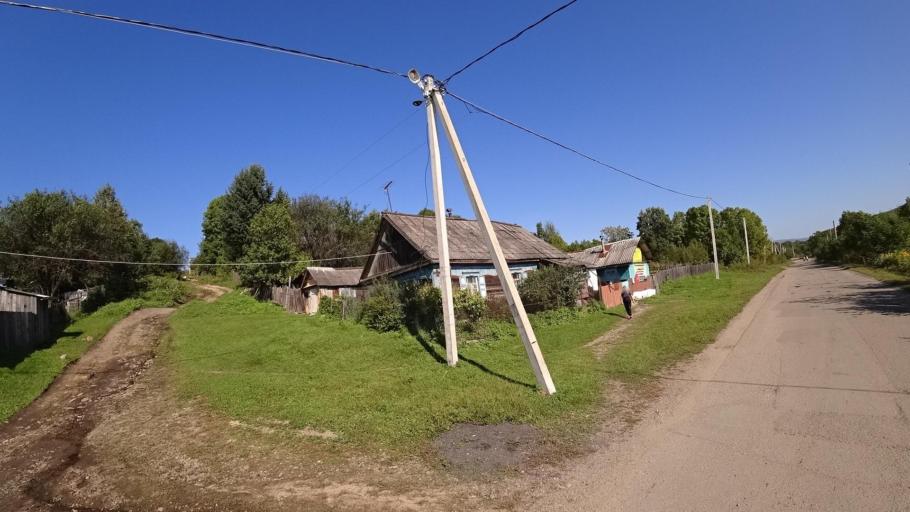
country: RU
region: Jewish Autonomous Oblast
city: Bira
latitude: 49.0085
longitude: 132.4723
